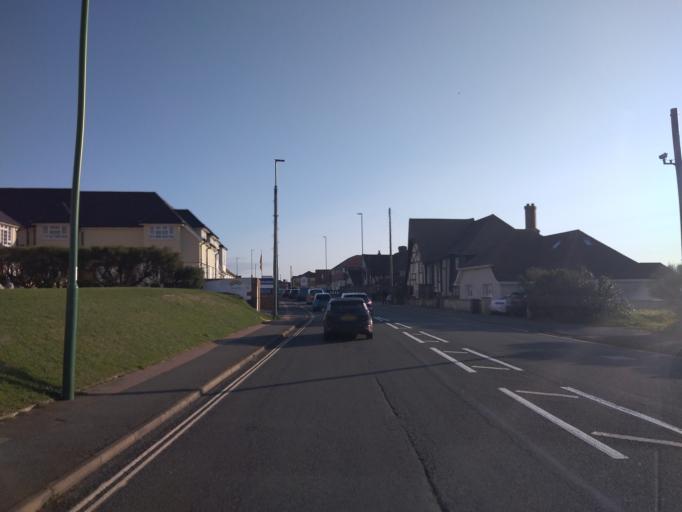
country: GB
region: England
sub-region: West Sussex
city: Lancing
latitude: 50.8184
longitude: -0.3313
